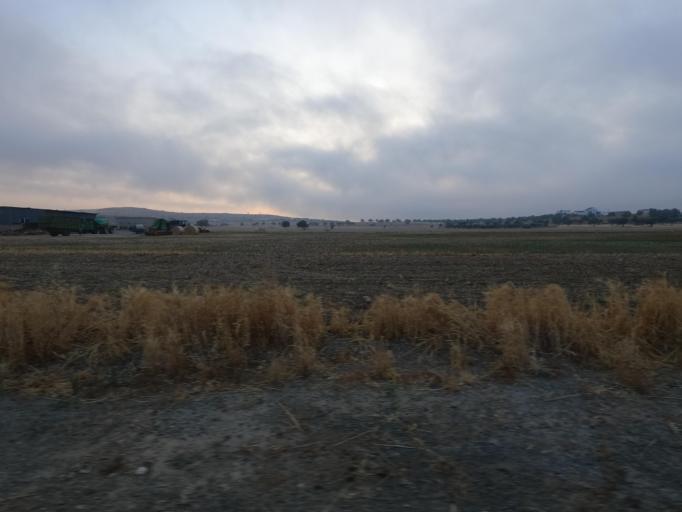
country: CY
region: Larnaka
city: Tersefanou
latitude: 34.8367
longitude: 33.5069
